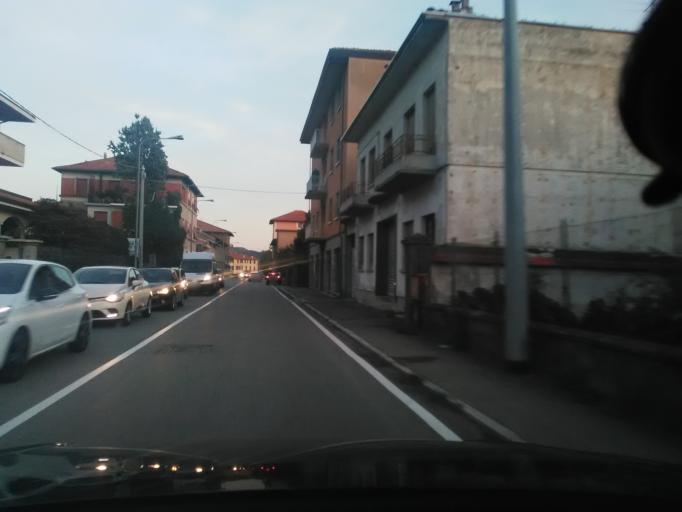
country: IT
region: Piedmont
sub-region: Provincia di Novara
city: Grignasco
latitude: 45.6831
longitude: 8.3348
